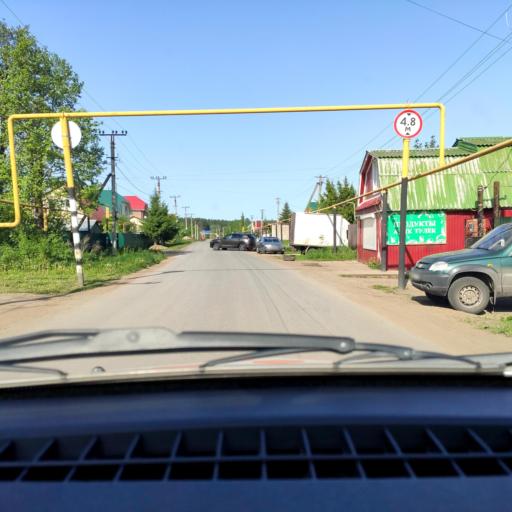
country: RU
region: Bashkortostan
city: Iglino
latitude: 54.8389
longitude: 56.2069
